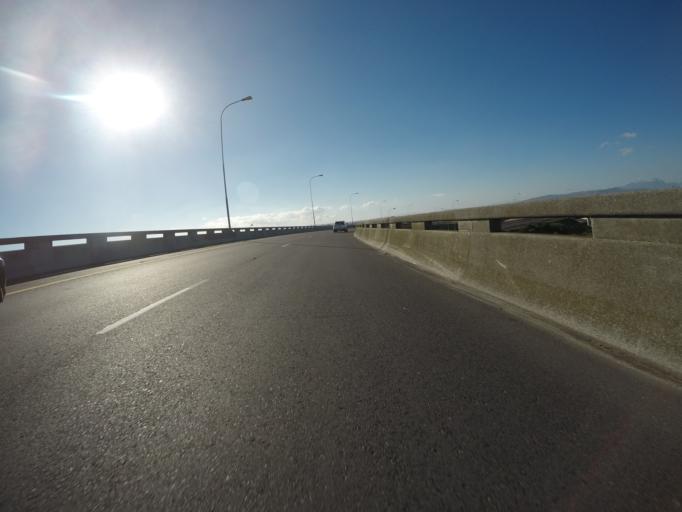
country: ZA
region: Western Cape
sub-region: City of Cape Town
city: Lansdowne
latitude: -34.0006
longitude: 18.6329
